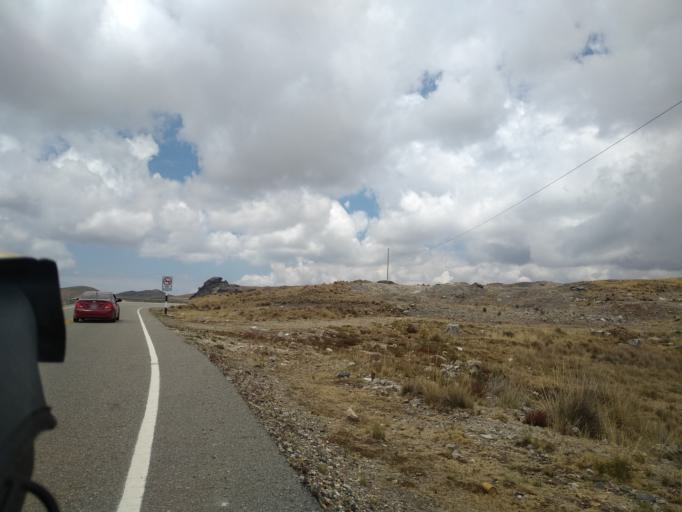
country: PE
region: La Libertad
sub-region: Provincia de Santiago de Chuco
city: Quiruvilca
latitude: -7.9405
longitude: -78.1858
